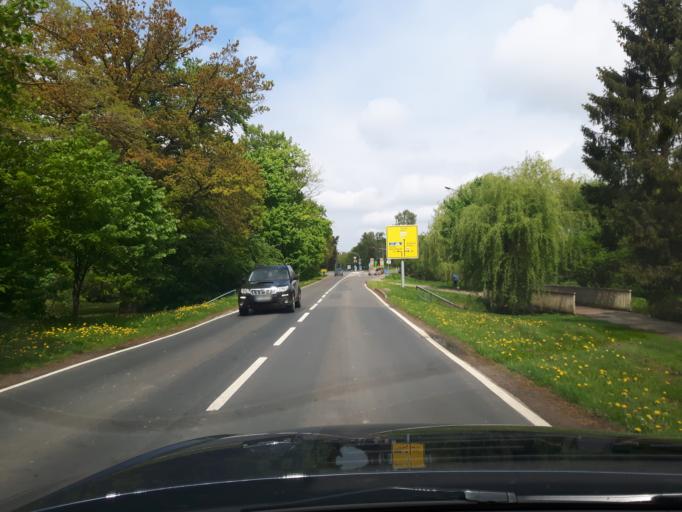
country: DE
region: Mecklenburg-Vorpommern
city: Barth
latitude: 54.2939
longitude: 12.7194
